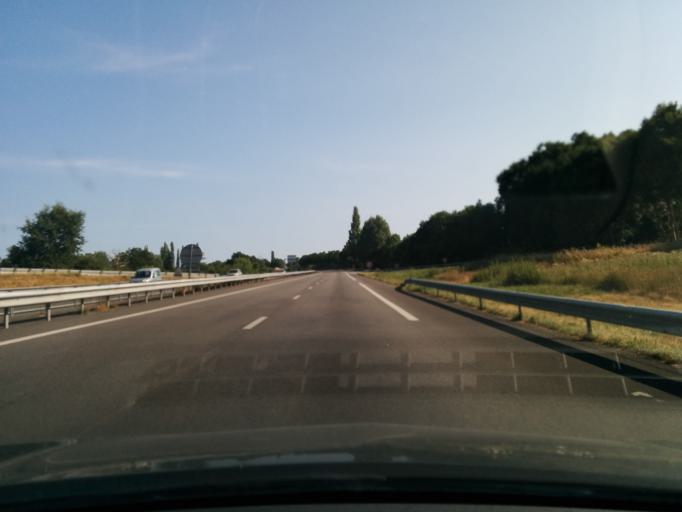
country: FR
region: Limousin
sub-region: Departement de la Haute-Vienne
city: Pierre-Buffiere
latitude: 45.6866
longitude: 1.3669
